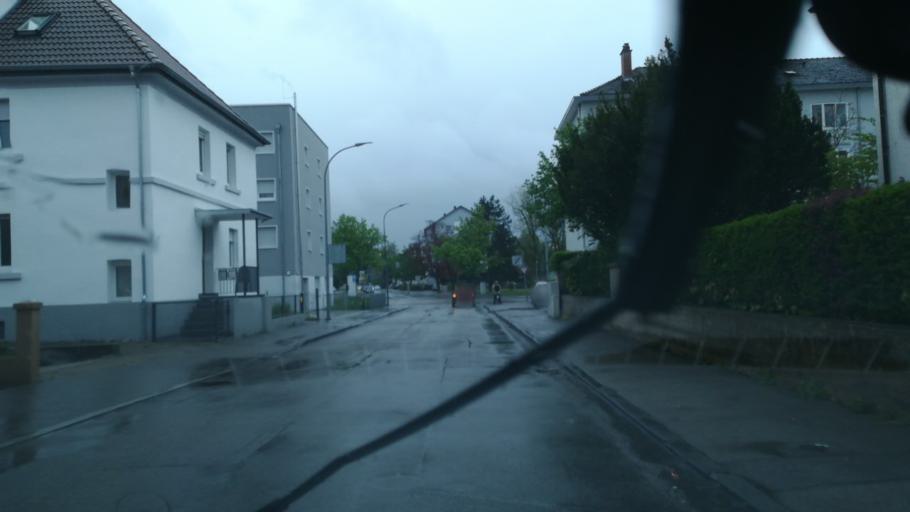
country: DE
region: Baden-Wuerttemberg
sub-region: Freiburg Region
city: Singen
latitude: 47.7522
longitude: 8.8428
